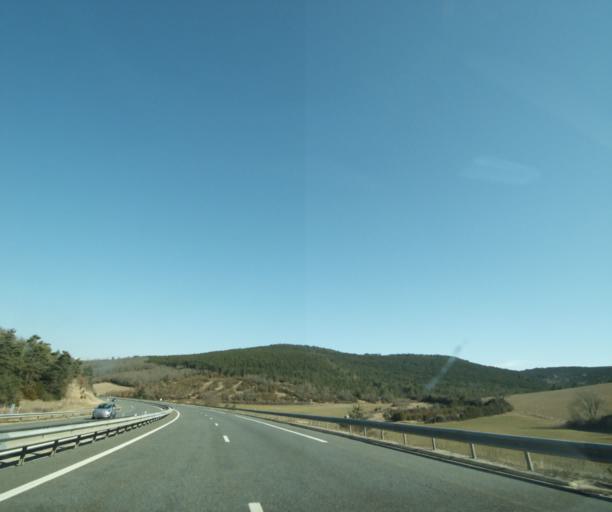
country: FR
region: Midi-Pyrenees
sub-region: Departement de l'Aveyron
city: Severac-le-Chateau
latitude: 44.3591
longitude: 3.1162
